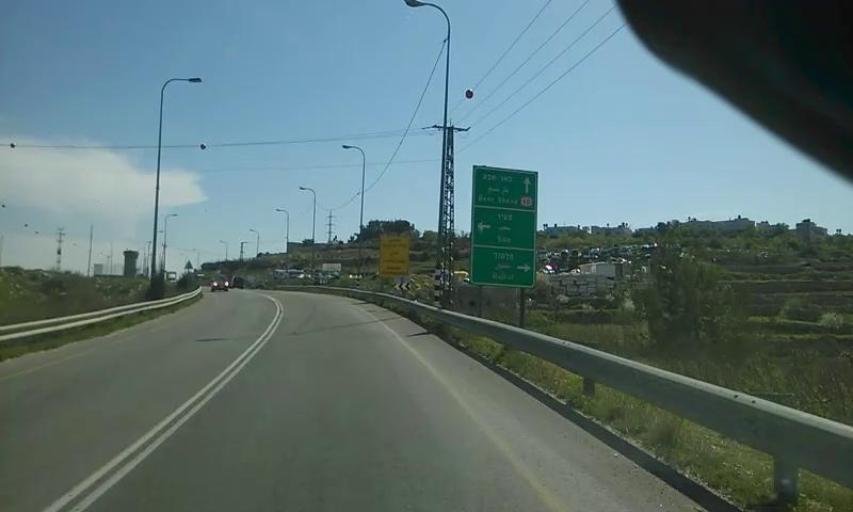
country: PS
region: West Bank
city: Halhul
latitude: 31.5855
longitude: 35.1189
